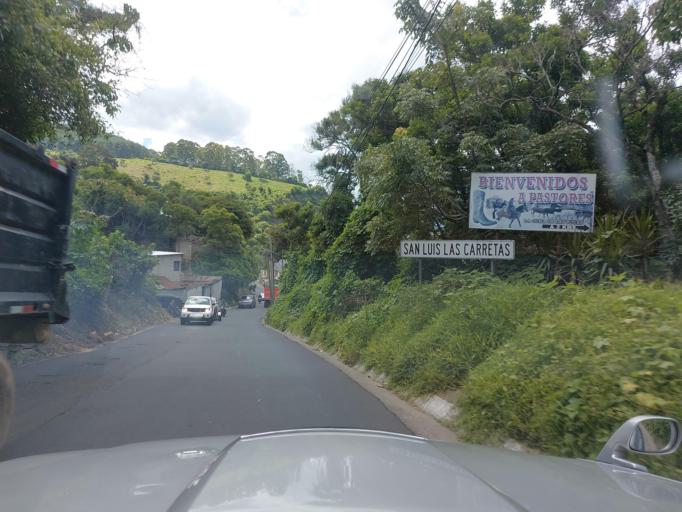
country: GT
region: Sacatepequez
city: Pastores
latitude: 14.6056
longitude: -90.7653
